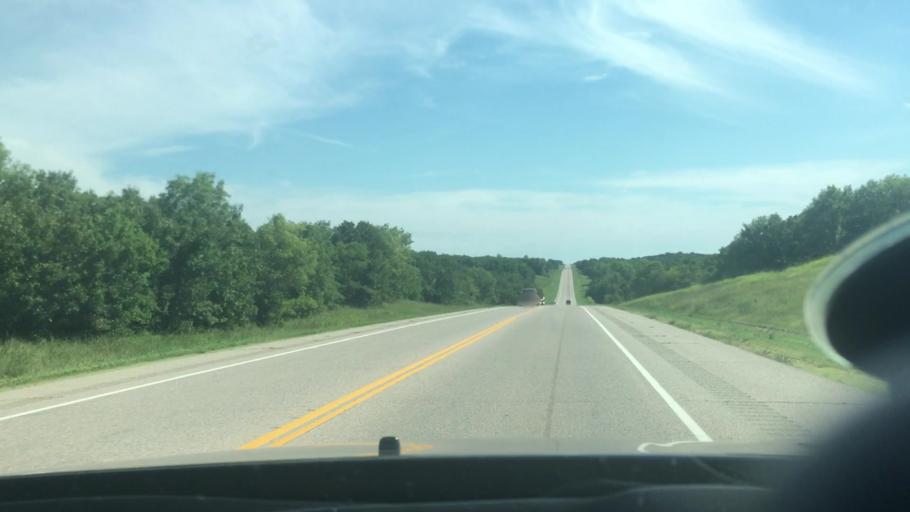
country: US
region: Oklahoma
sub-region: Seminole County
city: Maud
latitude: 35.1153
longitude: -96.6790
